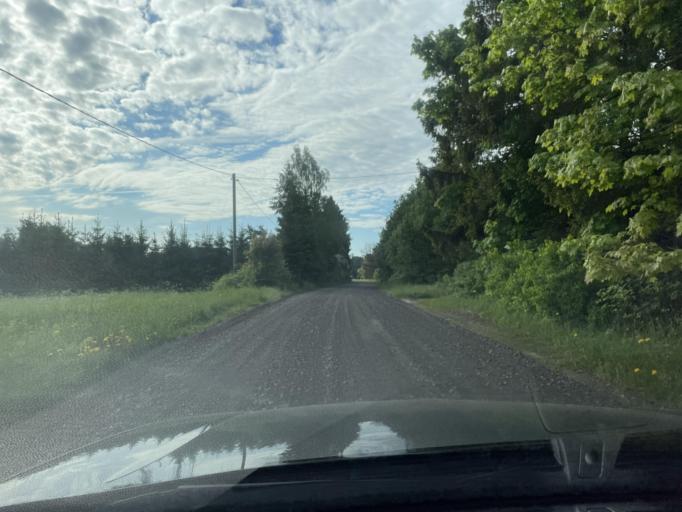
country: EE
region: Harju
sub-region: Keila linn
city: Keila
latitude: 59.2987
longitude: 24.3145
